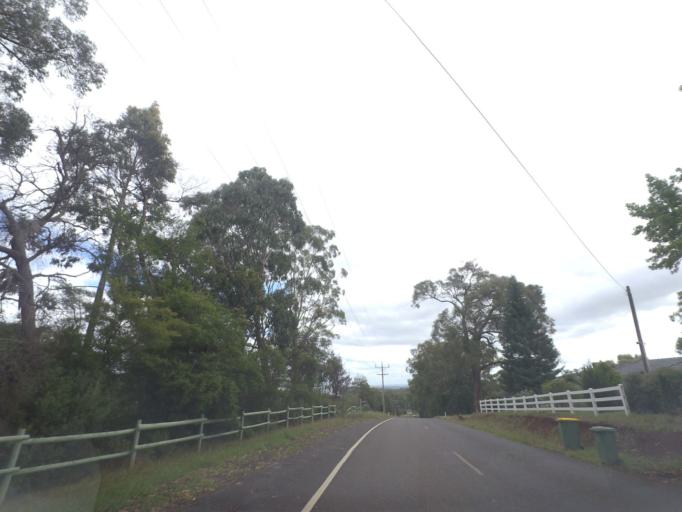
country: AU
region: Victoria
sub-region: Yarra Ranges
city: Launching Place
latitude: -37.8395
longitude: 145.5886
